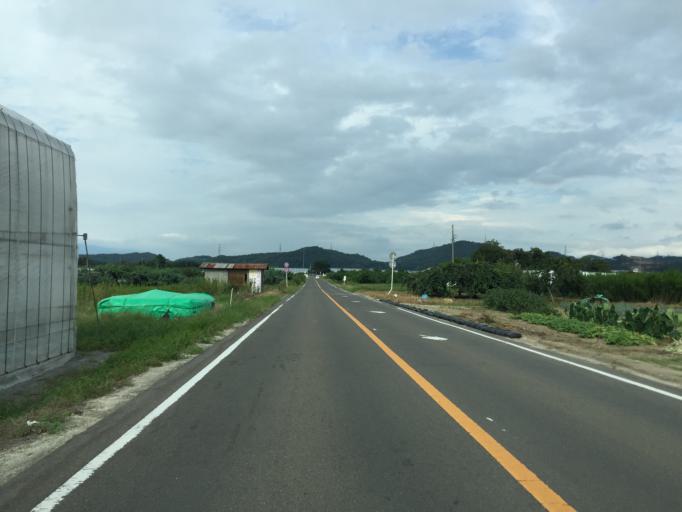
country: JP
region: Fukushima
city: Fukushima-shi
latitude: 37.7878
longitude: 140.4979
